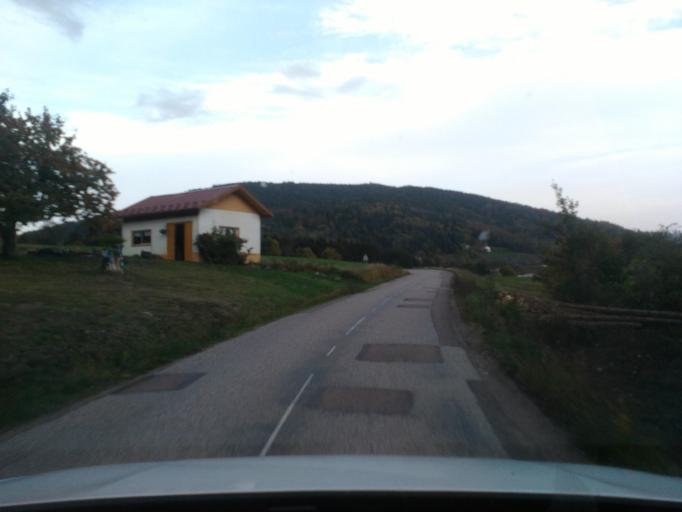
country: FR
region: Lorraine
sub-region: Departement des Vosges
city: Saint-Ame
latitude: 48.0418
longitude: 6.6726
